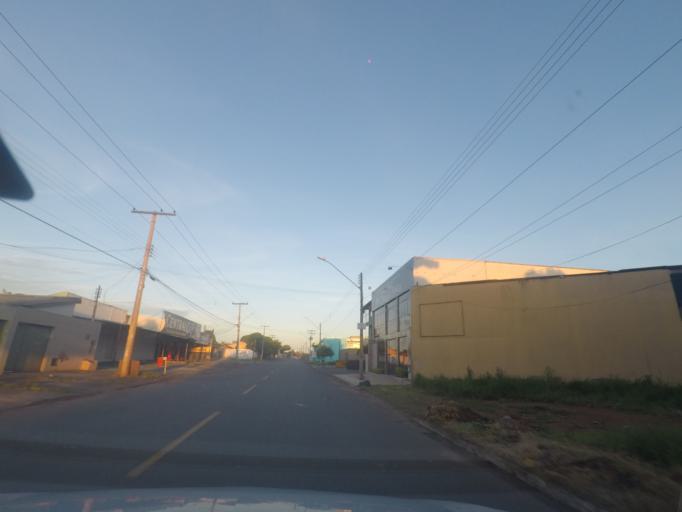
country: BR
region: Goias
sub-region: Goiania
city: Goiania
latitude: -16.6888
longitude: -49.3462
